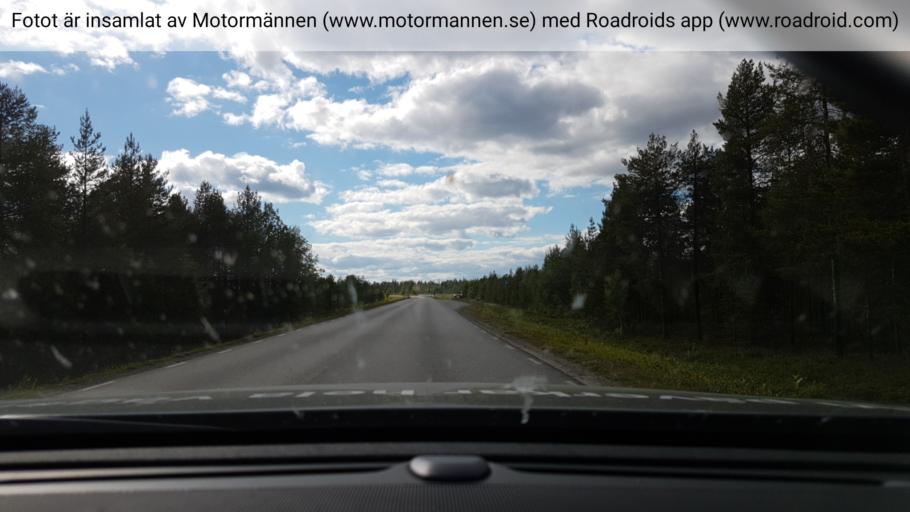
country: SE
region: Norrbotten
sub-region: Arjeplogs Kommun
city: Arjeplog
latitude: 66.0546
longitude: 17.8095
